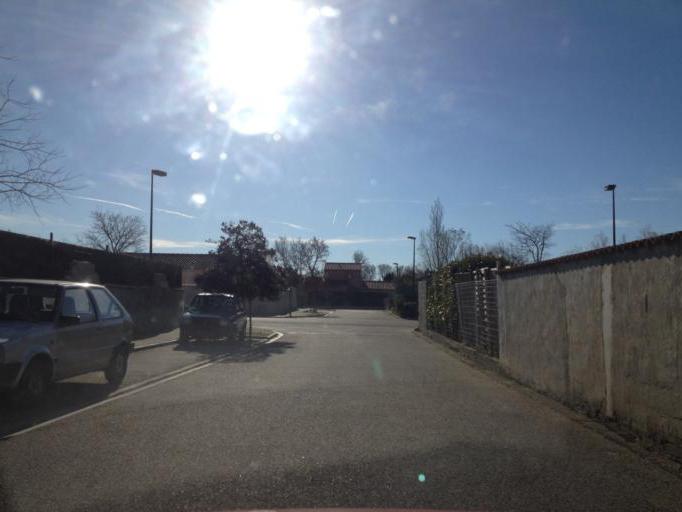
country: FR
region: Provence-Alpes-Cote d'Azur
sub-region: Departement du Vaucluse
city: Orange
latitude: 44.1457
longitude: 4.7963
